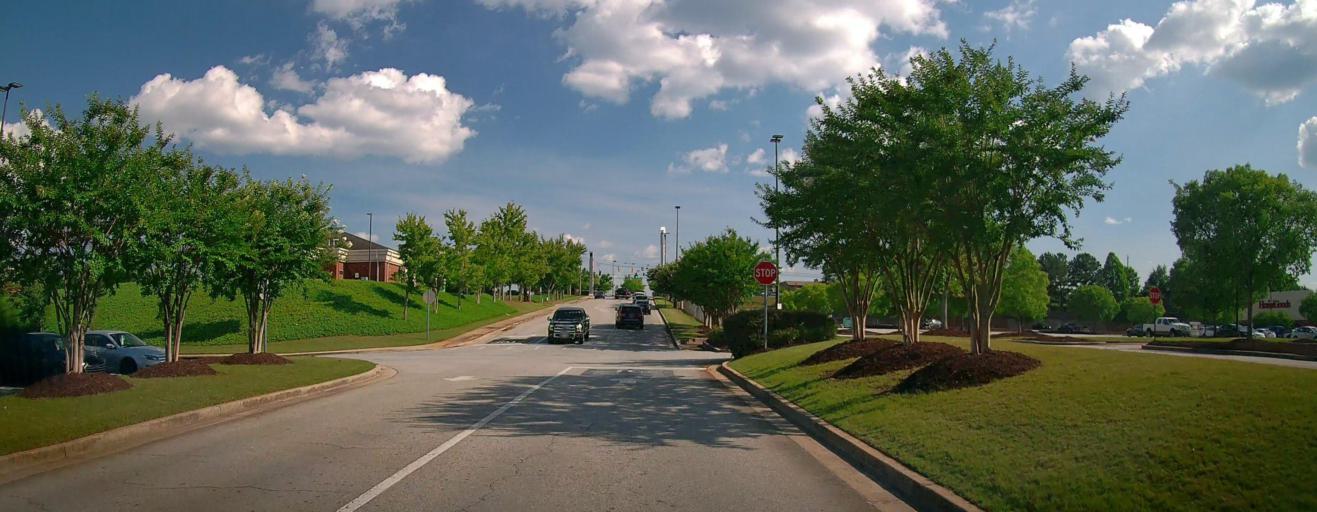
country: US
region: Georgia
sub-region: Henry County
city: McDonough
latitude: 33.4661
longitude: -84.2188
